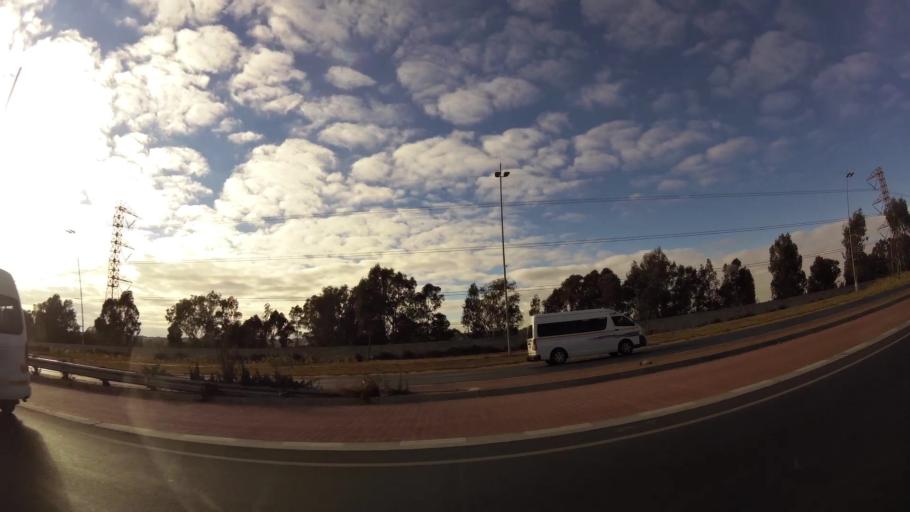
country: ZA
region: Gauteng
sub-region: City of Johannesburg Metropolitan Municipality
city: Modderfontein
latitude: -26.0452
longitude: 28.1876
